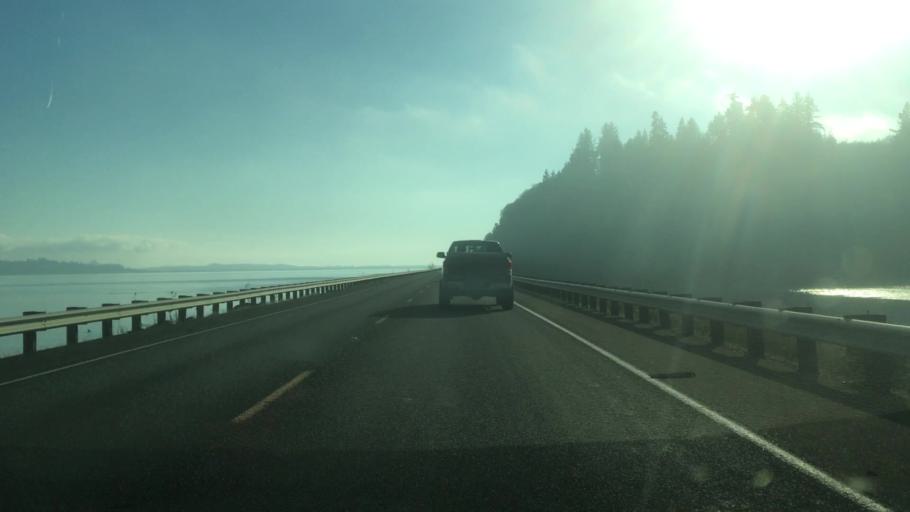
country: US
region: Oregon
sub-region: Clatsop County
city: Astoria
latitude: 46.2678
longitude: -123.8351
